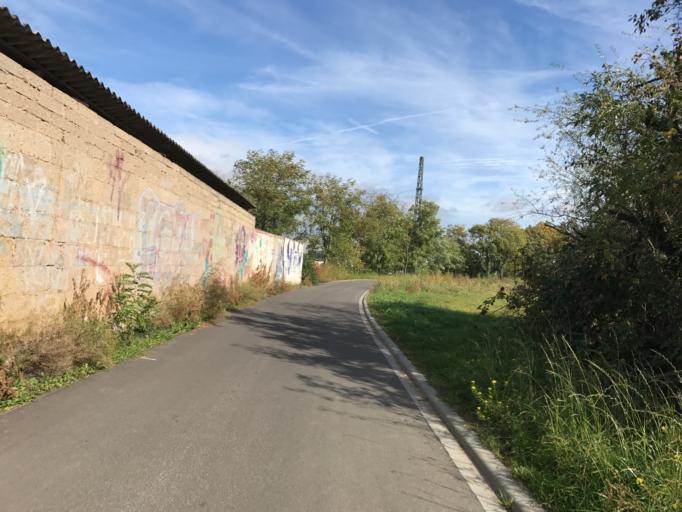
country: DE
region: Rheinland-Pfalz
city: Gau-Algesheim
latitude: 49.9637
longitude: 8.0236
